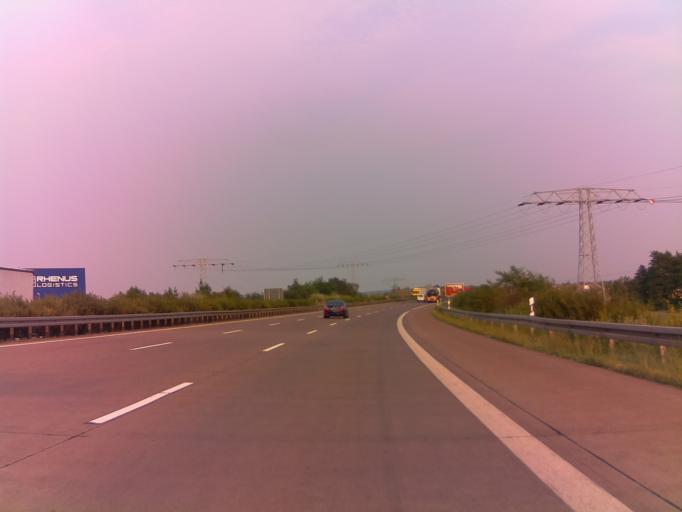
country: DE
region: Thuringia
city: Horselgau
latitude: 50.9192
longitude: 10.5676
